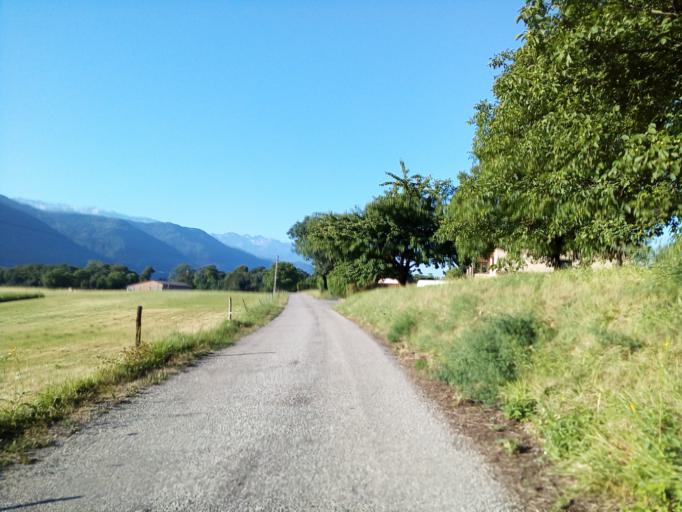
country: FR
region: Rhone-Alpes
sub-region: Departement de l'Isere
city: Le Cheylas
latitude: 45.3803
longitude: 5.9730
